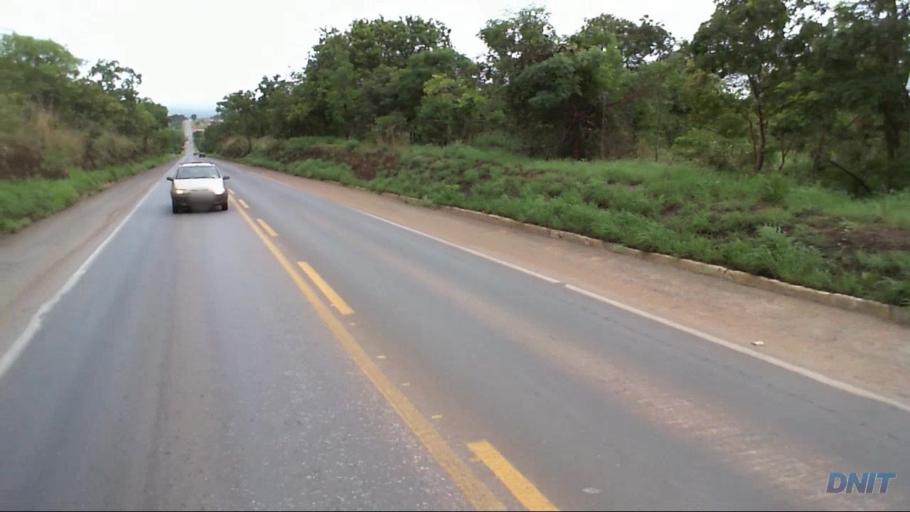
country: BR
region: Goias
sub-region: Uruacu
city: Uruacu
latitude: -14.5597
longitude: -49.1574
